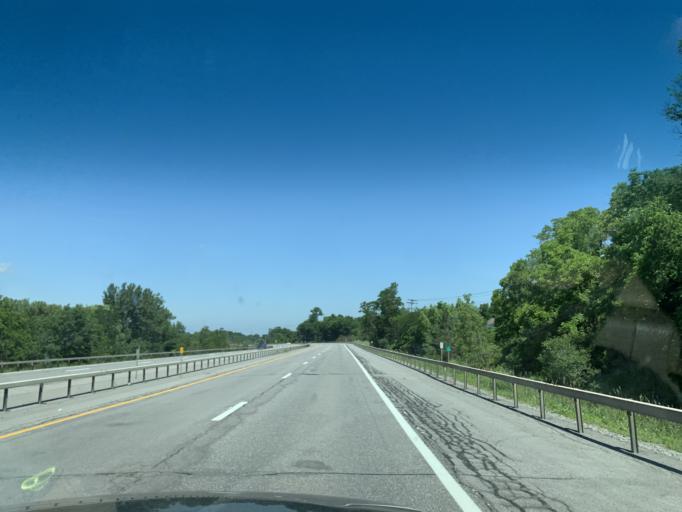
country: US
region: New York
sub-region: Oneida County
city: Chadwicks
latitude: 43.0386
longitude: -75.2714
